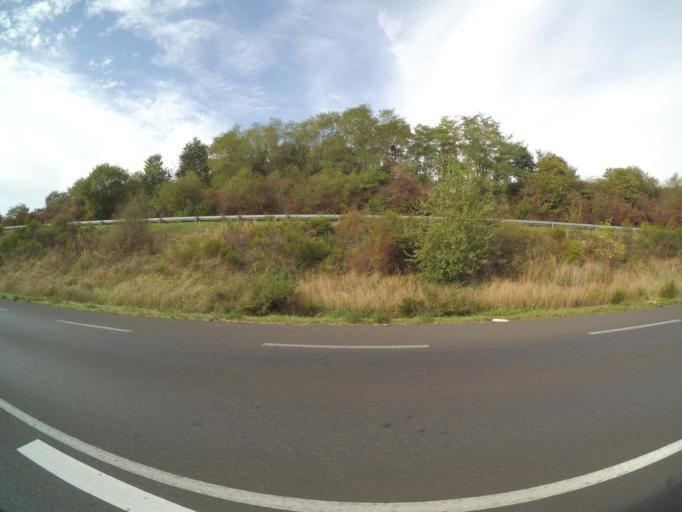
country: FR
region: Pays de la Loire
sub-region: Departement de Maine-et-Loire
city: Saumur
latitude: 47.2536
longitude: -0.1004
